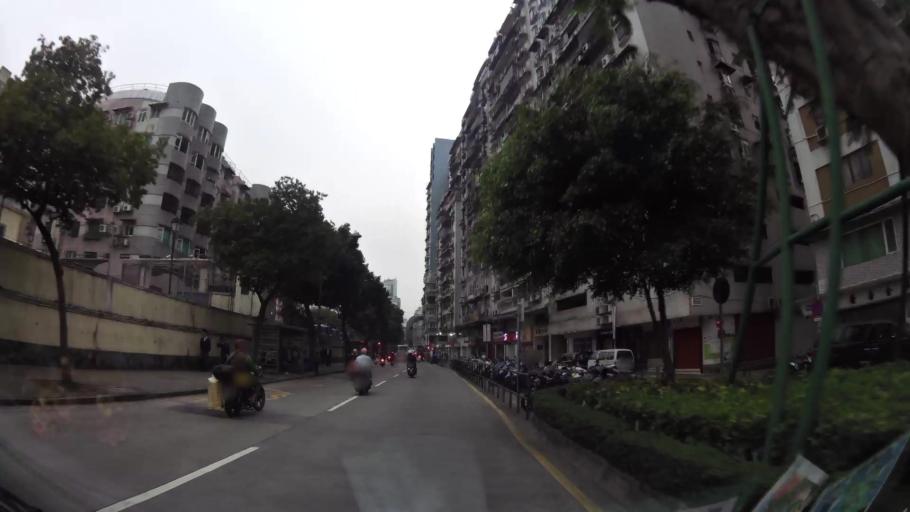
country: MO
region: Macau
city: Macau
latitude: 22.1996
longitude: 113.5491
